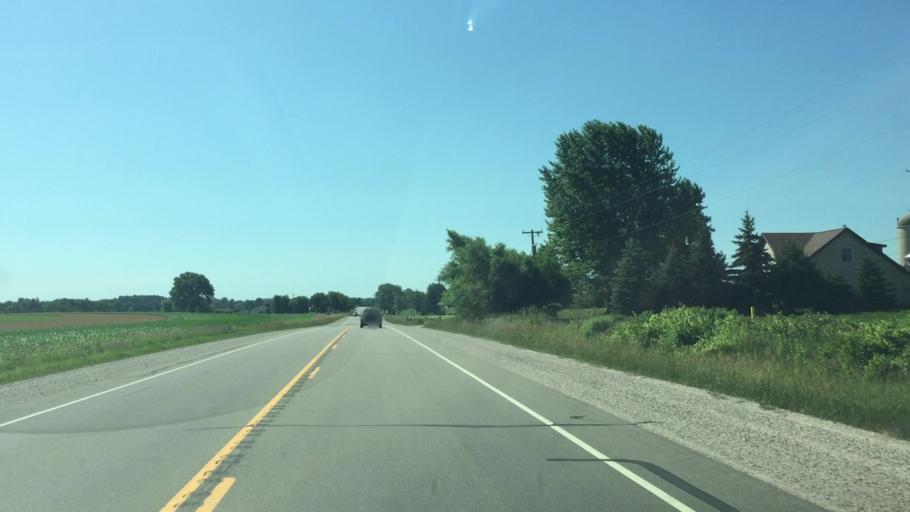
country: US
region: Wisconsin
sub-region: Calumet County
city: New Holstein
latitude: 43.9893
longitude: -88.1222
